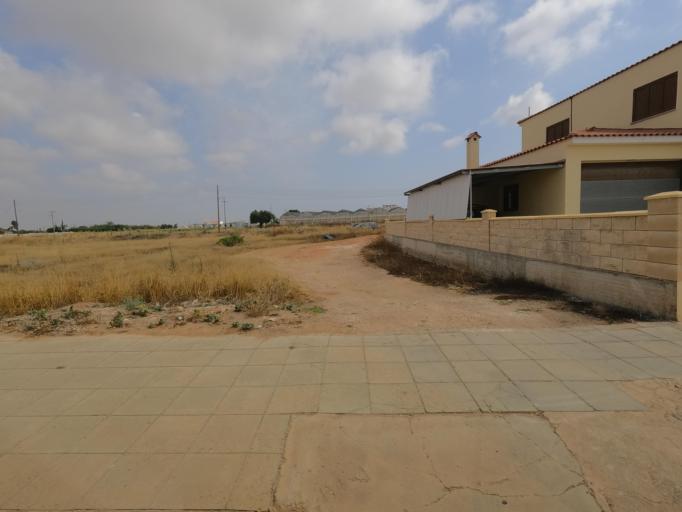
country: CY
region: Ammochostos
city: Deryneia
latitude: 35.0603
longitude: 33.9495
